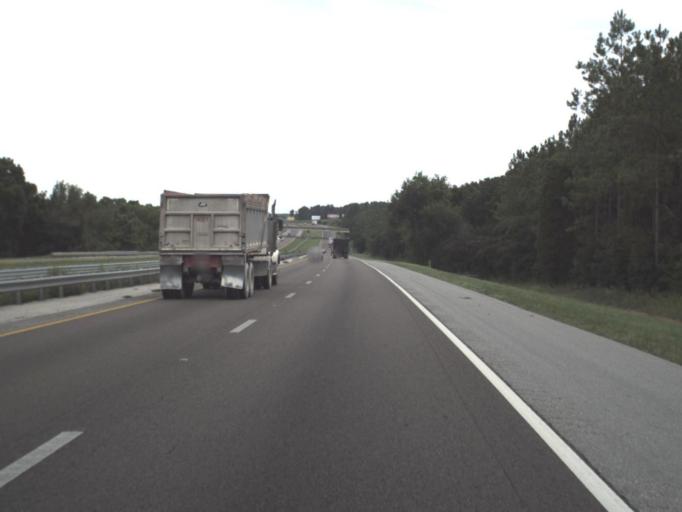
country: US
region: Florida
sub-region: Hernando County
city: Hill 'n Dale
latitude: 28.4745
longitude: -82.2586
